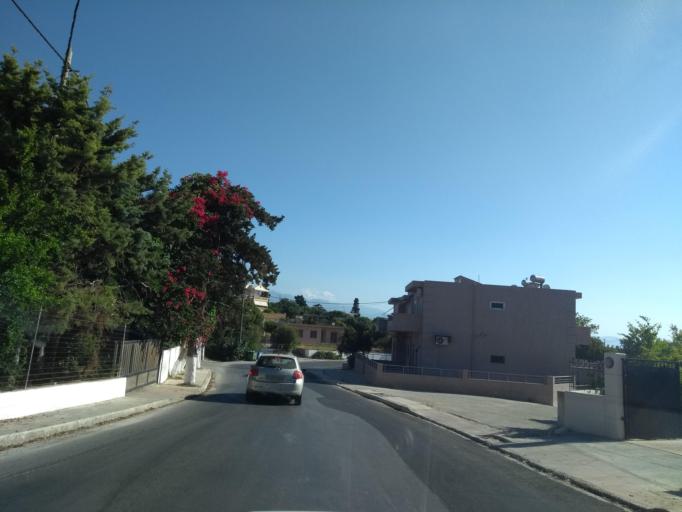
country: GR
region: Crete
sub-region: Nomos Chanias
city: Pithari
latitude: 35.5608
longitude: 24.0920
